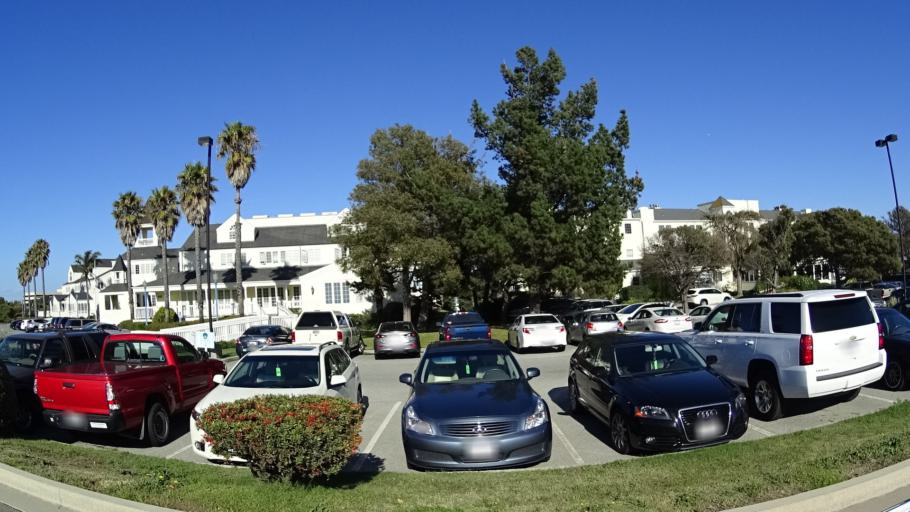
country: US
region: California
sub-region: San Mateo County
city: Brisbane
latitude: 37.6621
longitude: -122.3844
